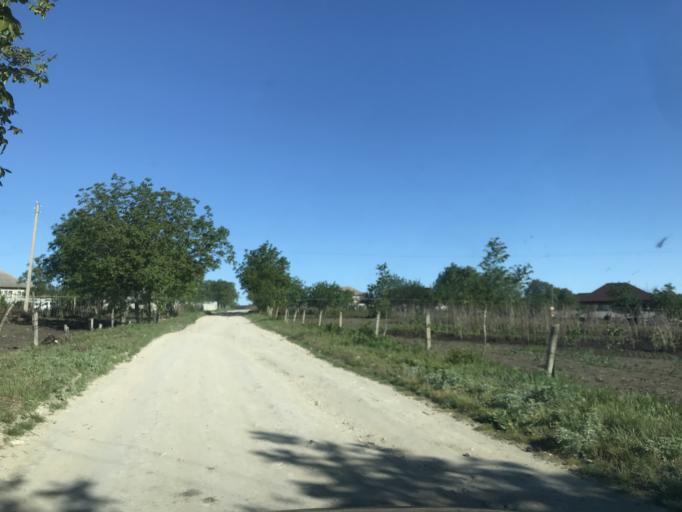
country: MD
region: Chisinau
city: Cricova
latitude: 47.2335
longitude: 28.8180
